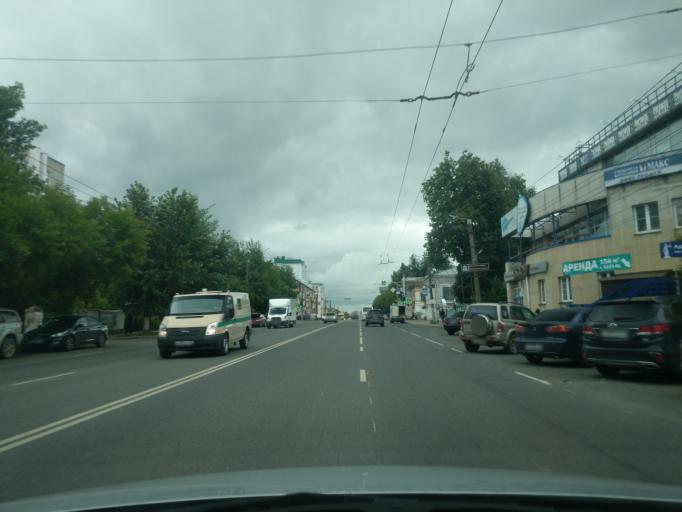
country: RU
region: Kirov
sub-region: Kirovo-Chepetskiy Rayon
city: Kirov
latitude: 58.5972
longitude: 49.6814
